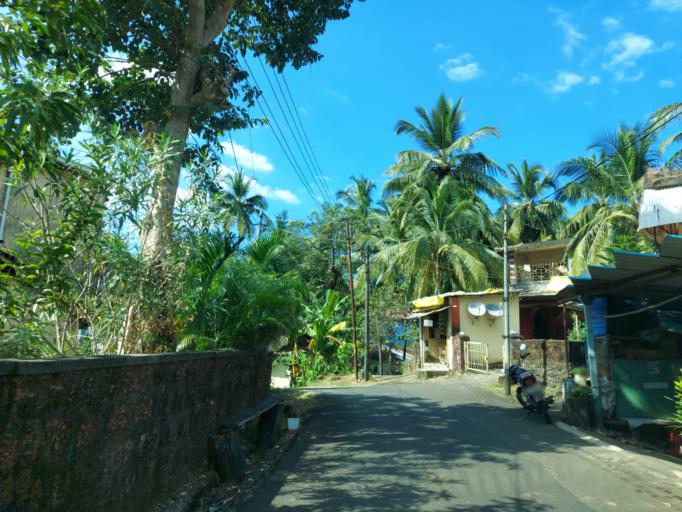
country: IN
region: Maharashtra
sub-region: Sindhudurg
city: Savantvadi
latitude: 15.9046
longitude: 73.8166
